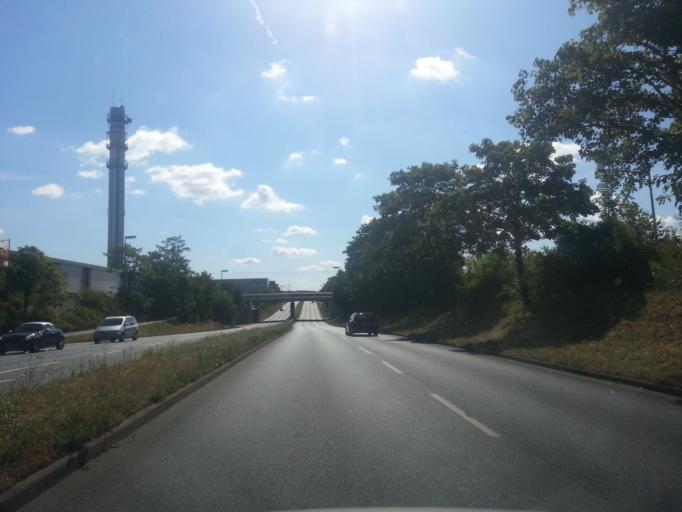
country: DE
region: Hesse
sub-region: Regierungsbezirk Darmstadt
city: Dietzenbach
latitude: 50.0166
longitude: 8.7864
